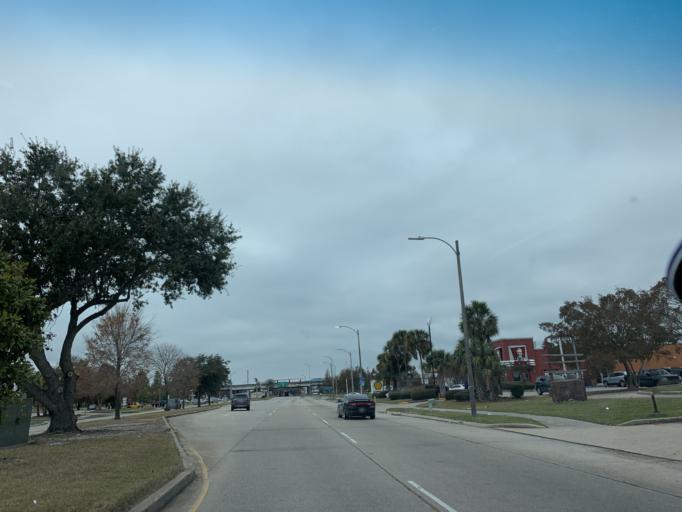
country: US
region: Louisiana
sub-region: Saint Bernard Parish
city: Arabi
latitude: 30.0440
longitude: -89.9592
